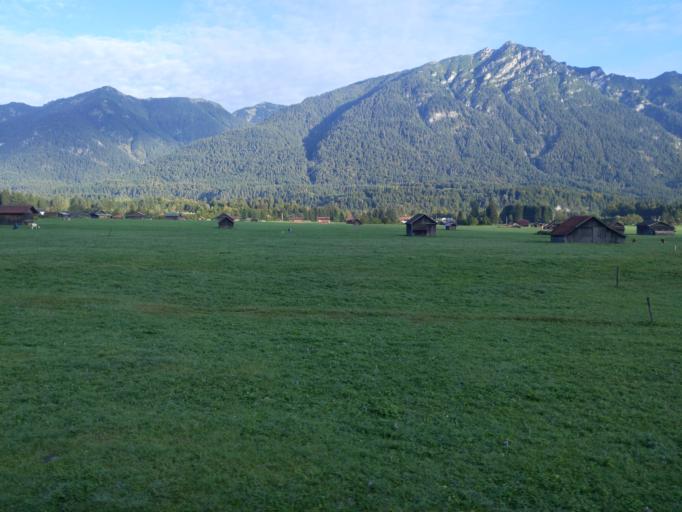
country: DE
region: Bavaria
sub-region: Upper Bavaria
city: Grainau
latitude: 47.4697
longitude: 11.0559
